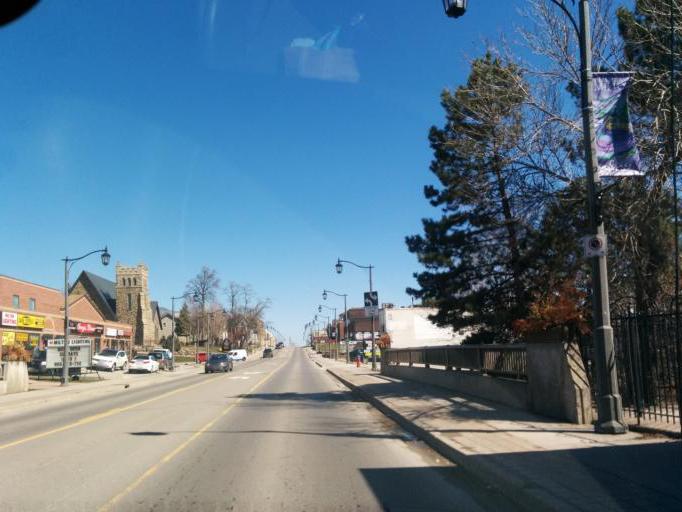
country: CA
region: Ontario
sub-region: Halton
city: Milton
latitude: 43.5149
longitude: -79.8812
